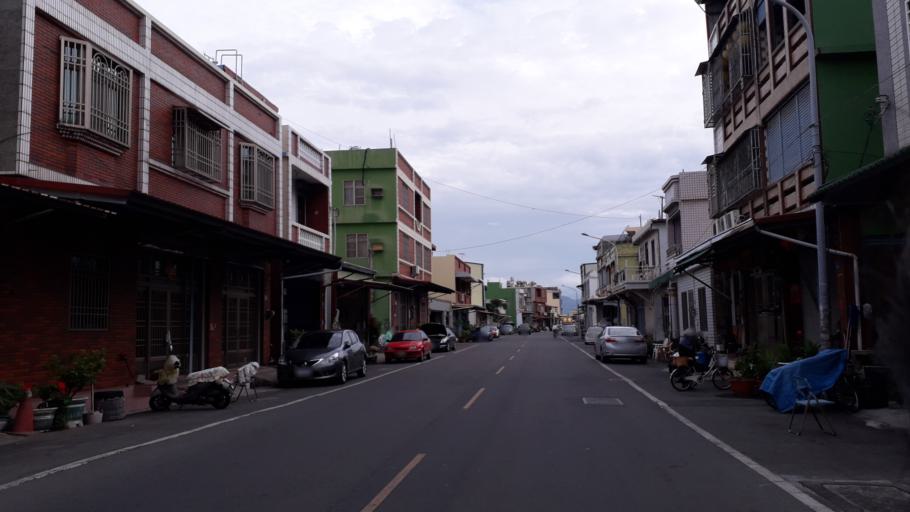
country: TW
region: Taiwan
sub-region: Pingtung
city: Pingtung
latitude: 22.3609
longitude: 120.5967
